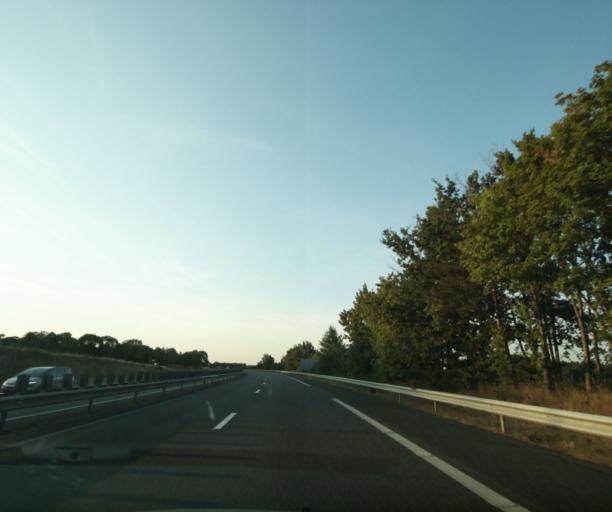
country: FR
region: Aquitaine
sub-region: Departement du Lot-et-Garonne
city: Boe
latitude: 44.1553
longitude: 0.6187
